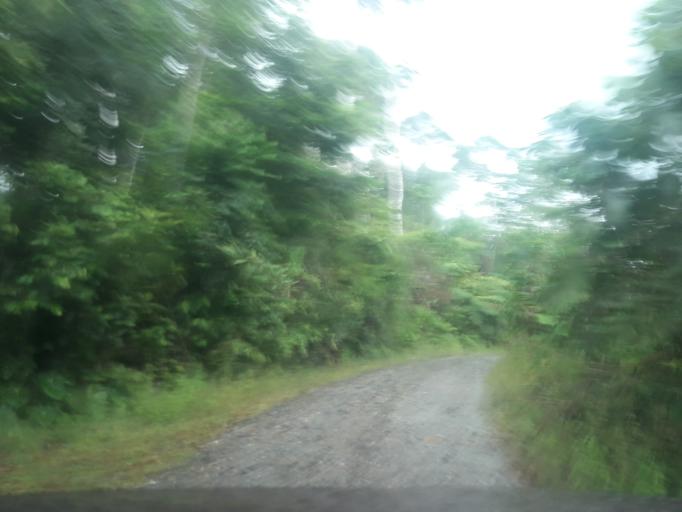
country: EC
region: Napo
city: Tena
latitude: -1.0981
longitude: -77.6956
